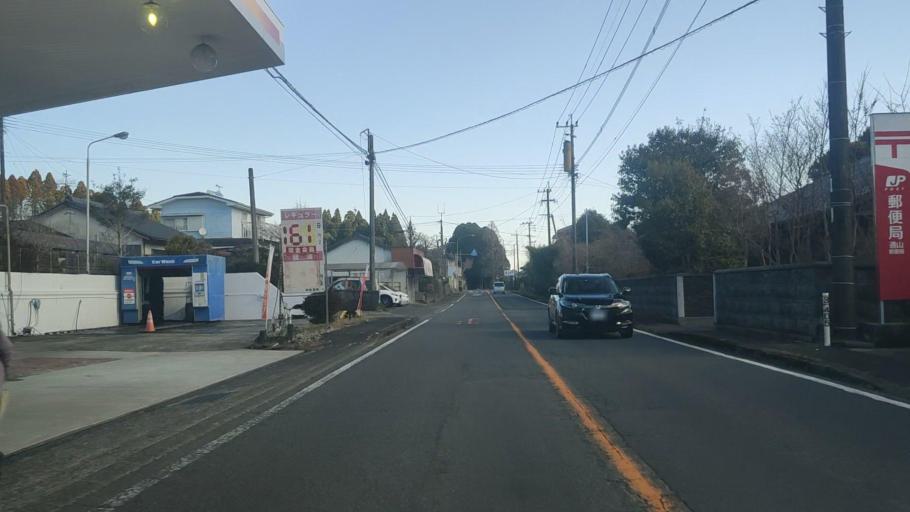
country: JP
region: Kagoshima
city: Sueyoshicho-ninokata
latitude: 31.6840
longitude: 130.9416
